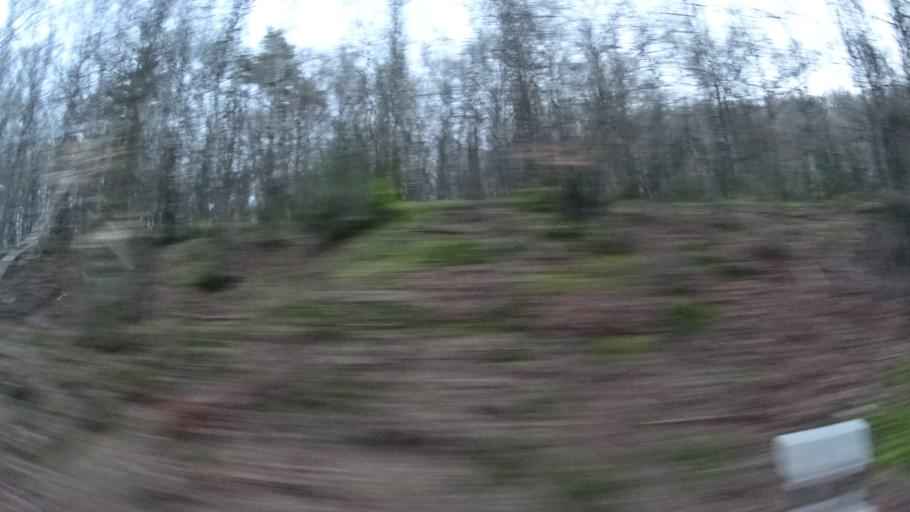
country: DE
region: Rheinland-Pfalz
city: Dambach
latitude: 49.6196
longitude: 7.1276
